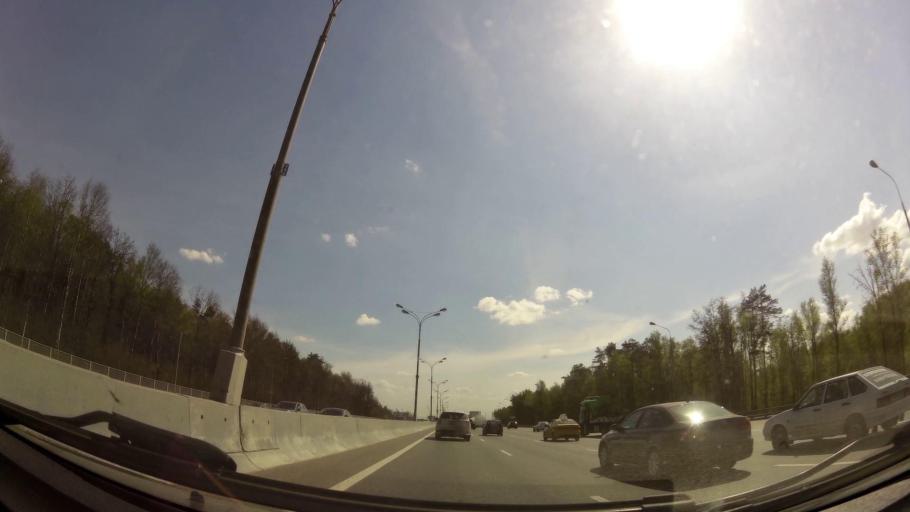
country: RU
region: Moskovskaya
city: Nemchinovka
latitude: 55.7399
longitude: 37.3724
